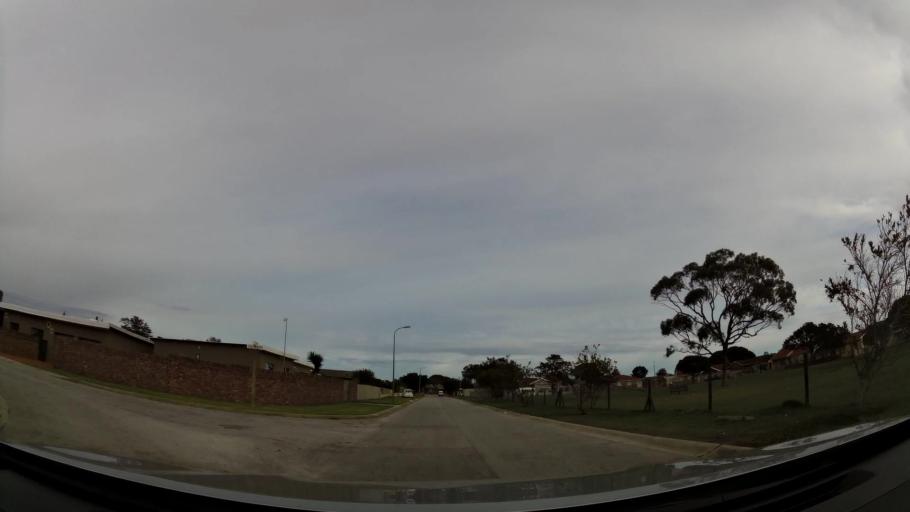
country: ZA
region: Eastern Cape
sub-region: Nelson Mandela Bay Metropolitan Municipality
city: Port Elizabeth
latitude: -33.9418
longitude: 25.4993
